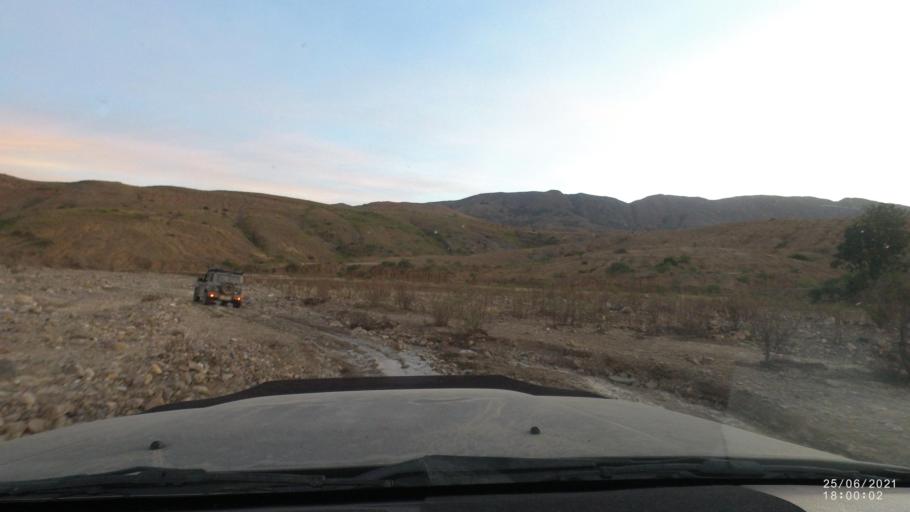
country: BO
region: Cochabamba
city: Mizque
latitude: -17.9452
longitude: -65.6348
